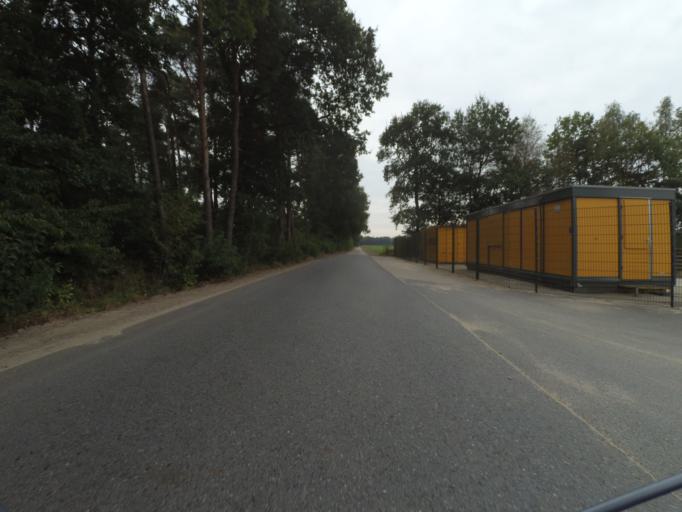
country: NL
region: Overijssel
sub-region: Gemeente Losser
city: Losser
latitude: 52.2802
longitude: 7.0420
